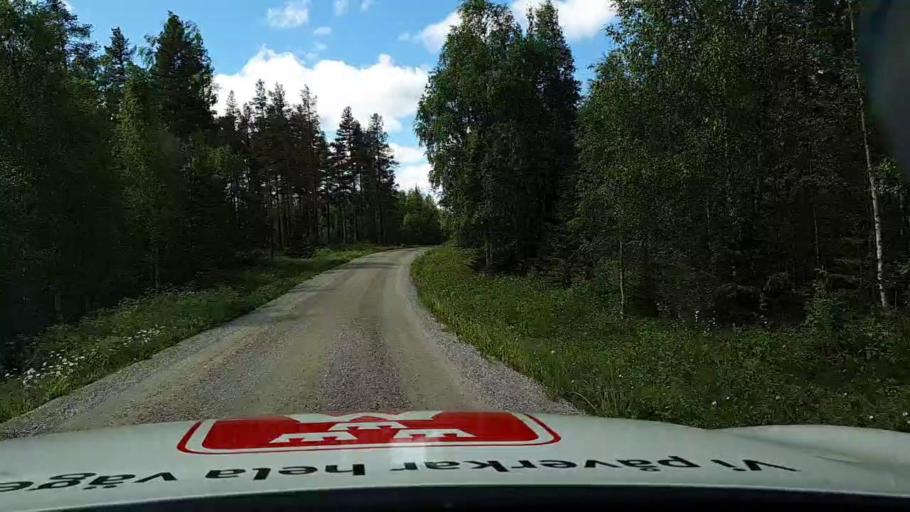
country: SE
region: Jaemtland
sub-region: Braecke Kommun
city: Braecke
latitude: 62.7400
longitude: 15.4939
